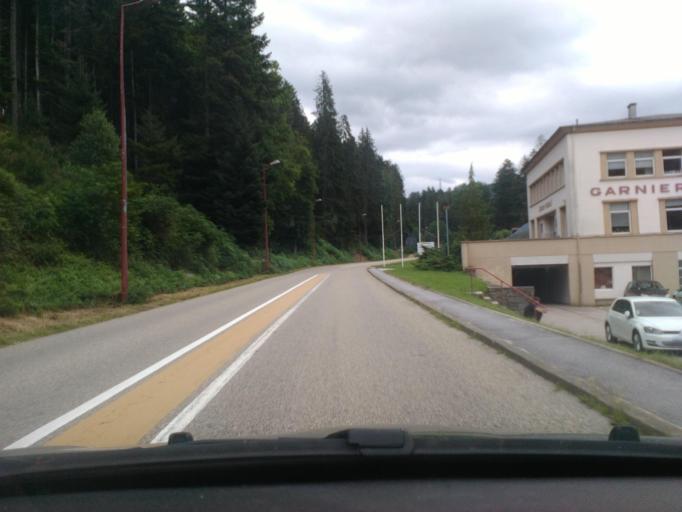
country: FR
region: Lorraine
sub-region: Departement des Vosges
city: Gerardmer
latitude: 48.0902
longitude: 6.8889
